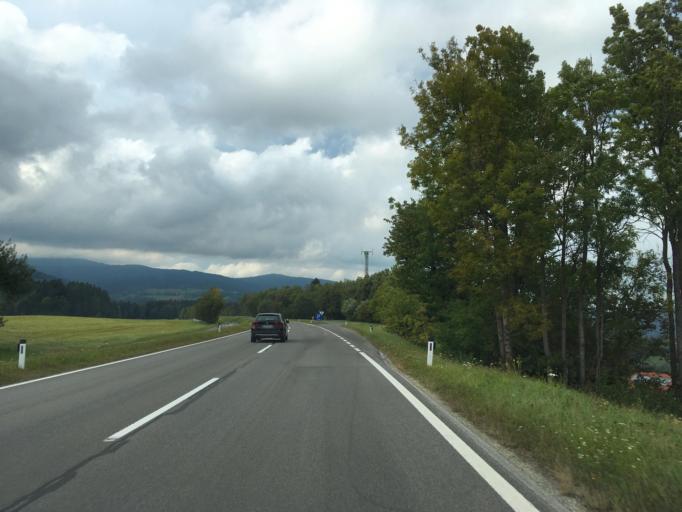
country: AT
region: Styria
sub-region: Politischer Bezirk Hartberg-Fuerstenfeld
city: Pinggau
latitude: 47.4676
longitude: 16.0592
